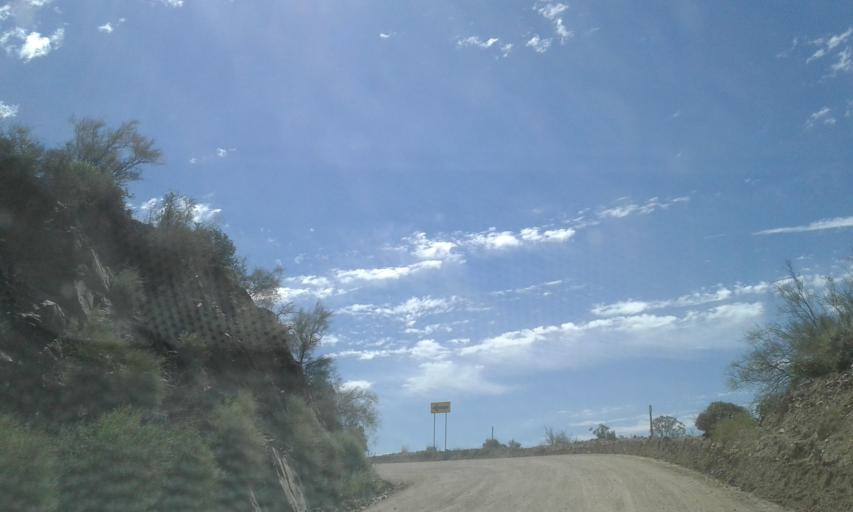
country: US
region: Arizona
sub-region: Gila County
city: Tonto Basin
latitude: 33.6066
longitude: -111.1983
